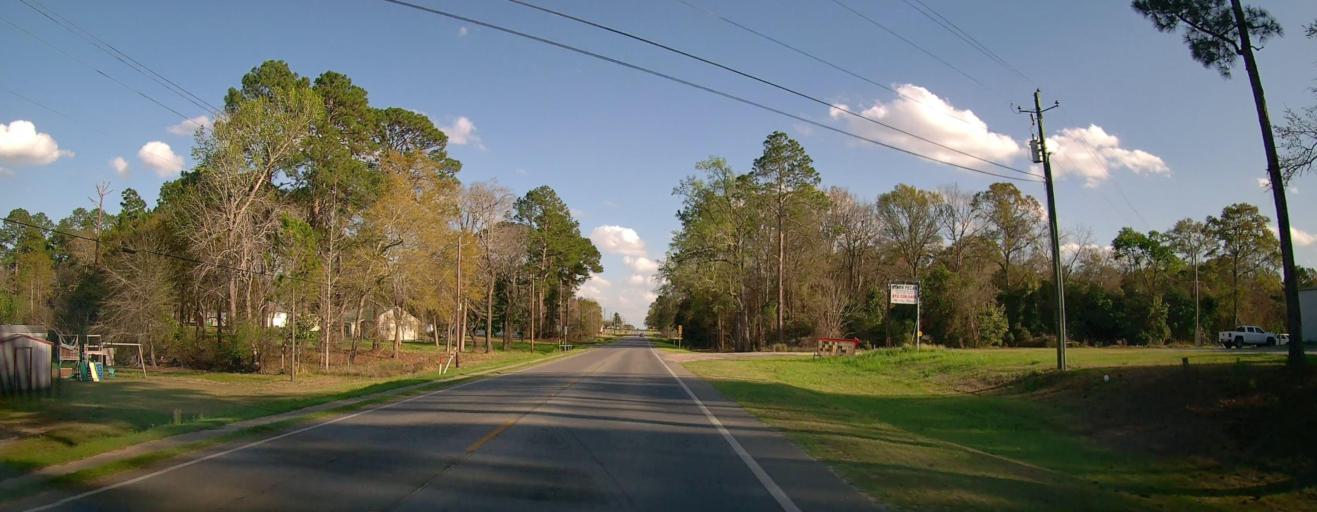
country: US
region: Georgia
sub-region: Toombs County
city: Lyons
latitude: 32.1993
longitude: -82.3148
